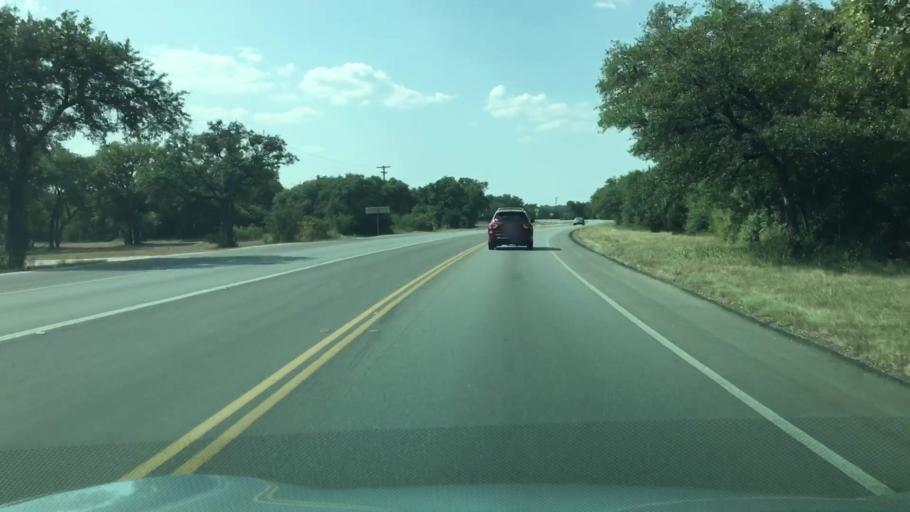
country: US
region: Texas
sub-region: Hays County
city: Wimberley
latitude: 29.9349
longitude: -98.0786
